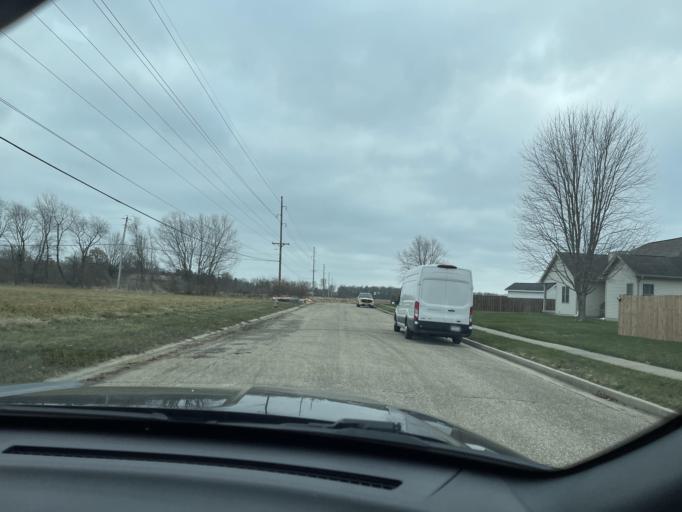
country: US
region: Illinois
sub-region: Sangamon County
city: Rochester
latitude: 39.7518
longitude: -89.5786
